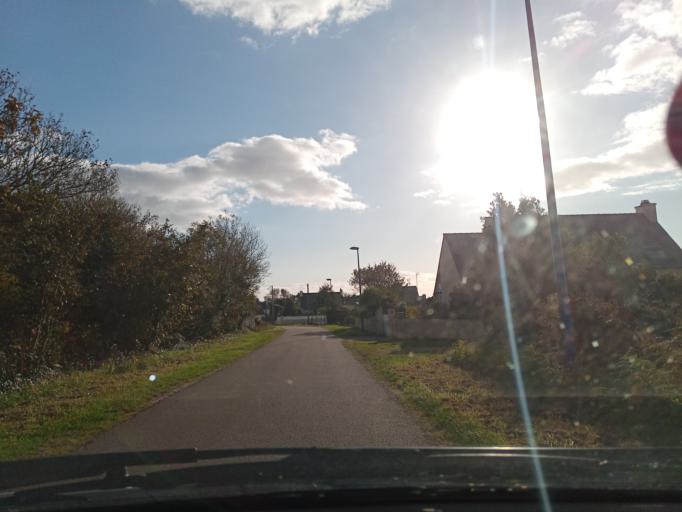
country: FR
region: Brittany
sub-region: Departement du Finistere
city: Audierne
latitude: 48.0205
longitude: -4.5138
